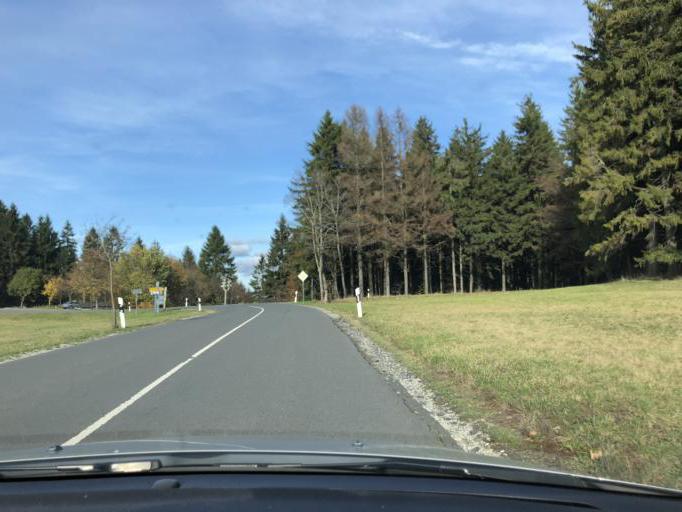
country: DE
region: Thuringia
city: Masserberg
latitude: 50.5116
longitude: 10.9255
